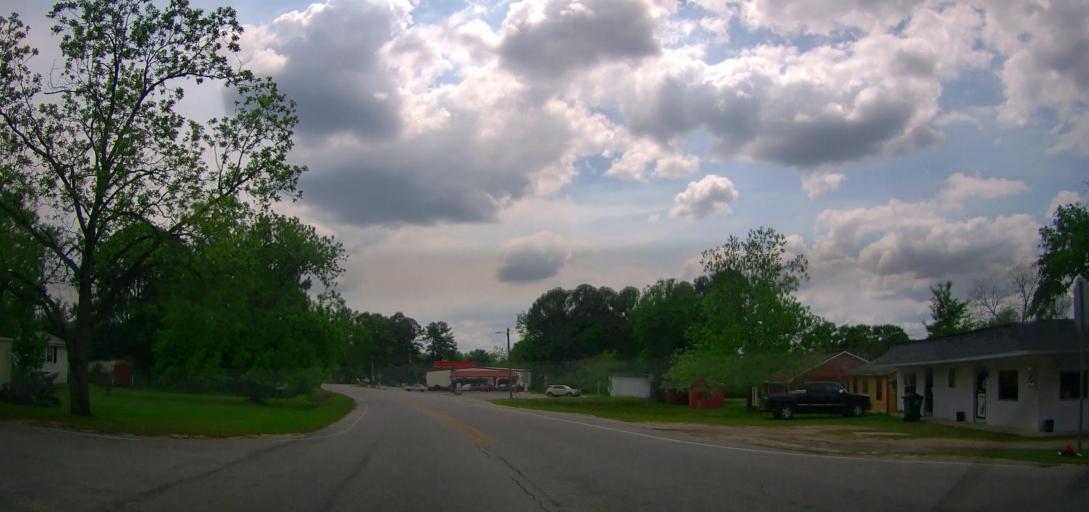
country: US
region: Georgia
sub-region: Treutlen County
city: Soperton
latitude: 32.3736
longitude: -82.5956
